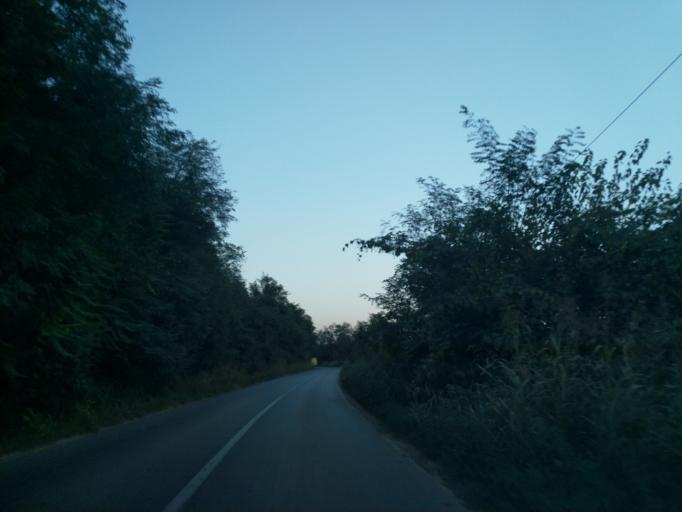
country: RS
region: Central Serbia
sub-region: Rasinski Okrug
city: Krusevac
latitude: 43.6026
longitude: 21.2678
